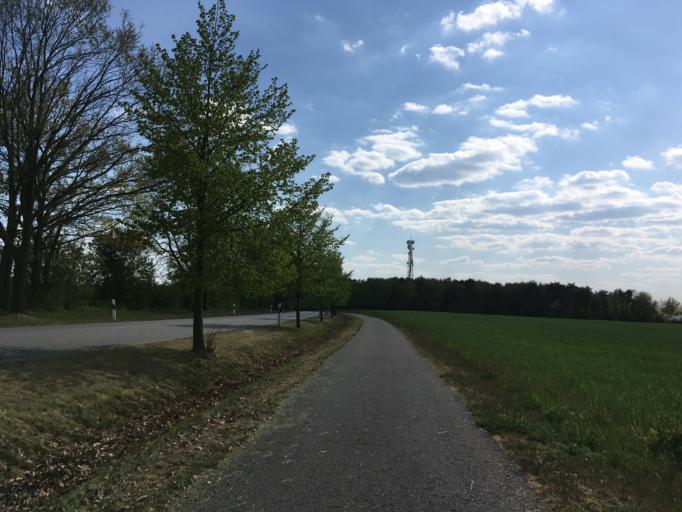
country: DE
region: Brandenburg
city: Ahrensfelde
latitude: 52.5928
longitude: 13.5653
